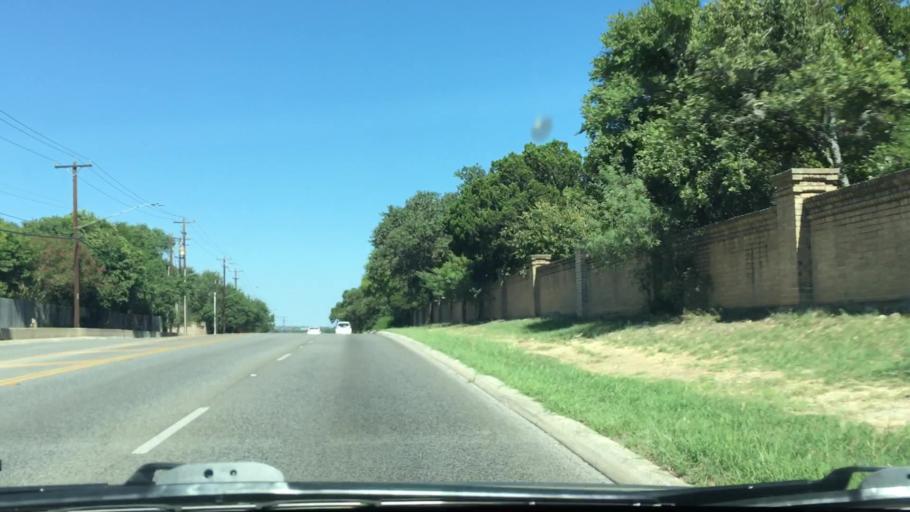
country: US
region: Texas
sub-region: Bexar County
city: Hollywood Park
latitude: 29.5740
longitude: -98.4940
